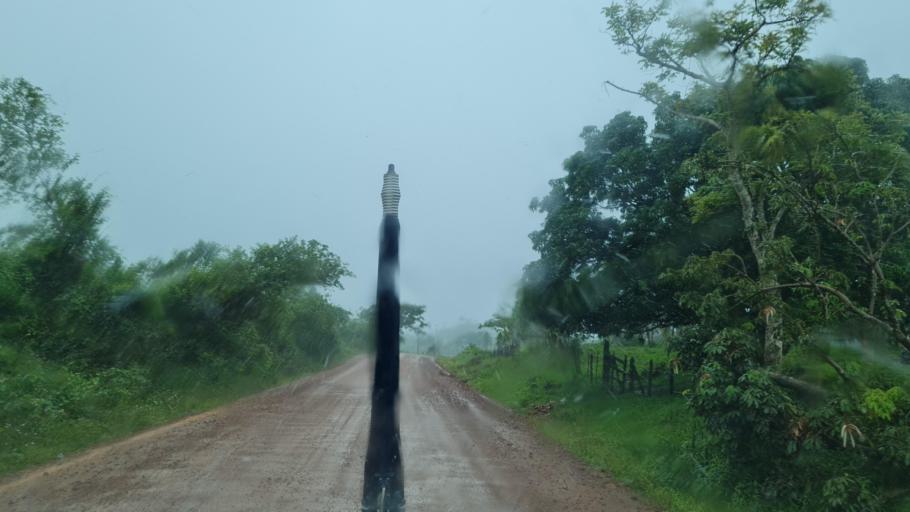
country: NI
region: Atlantico Norte (RAAN)
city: Puerto Cabezas
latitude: 14.0909
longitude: -83.8421
